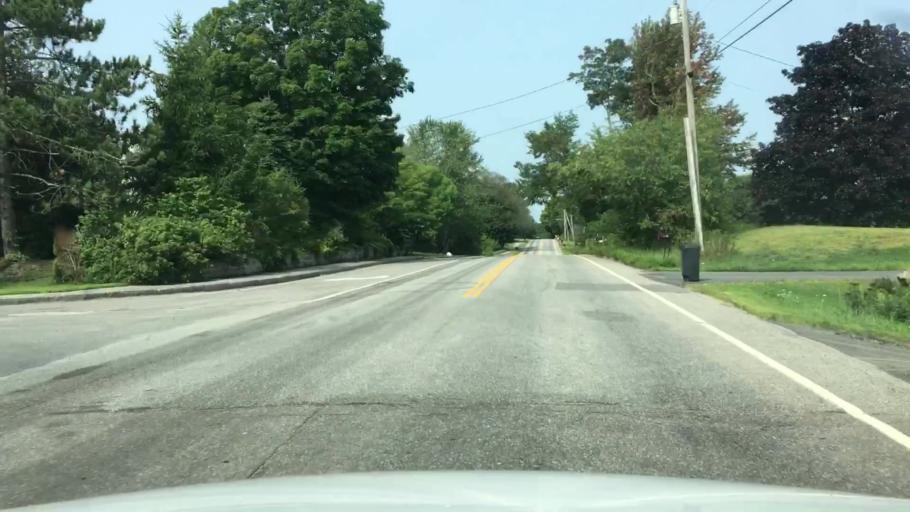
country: US
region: Maine
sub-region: Kennebec County
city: Augusta
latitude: 44.3191
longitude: -69.7434
